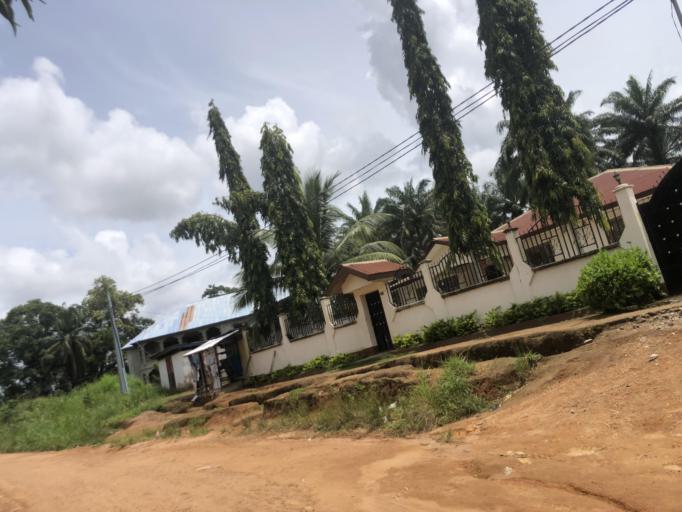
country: SL
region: Northern Province
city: Makeni
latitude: 8.8570
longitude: -12.0553
